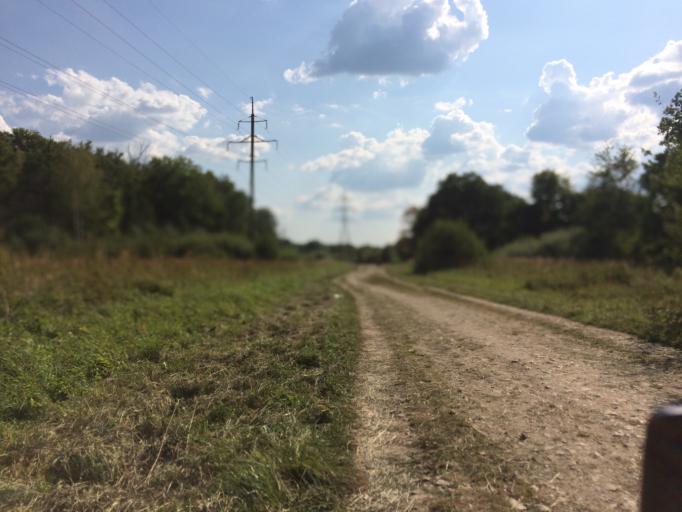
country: RU
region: Mariy-El
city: Yoshkar-Ola
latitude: 56.6169
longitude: 47.9311
